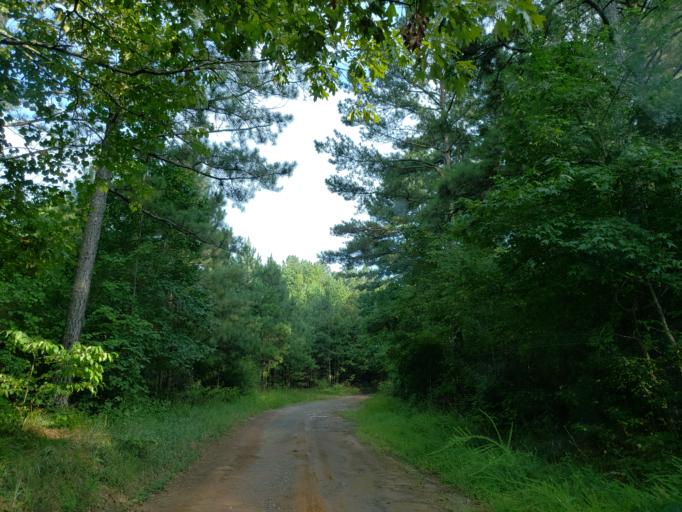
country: US
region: Georgia
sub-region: Bartow County
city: Emerson
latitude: 34.1864
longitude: -84.6467
